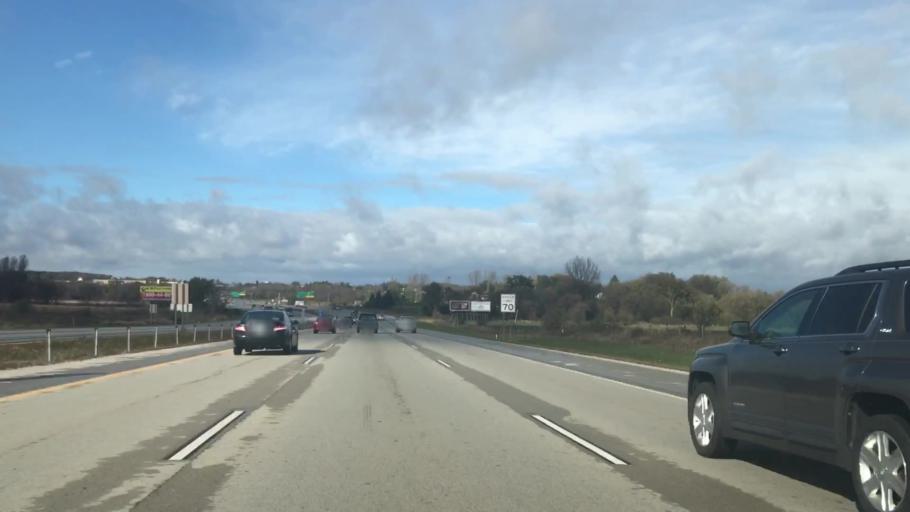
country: US
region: Wisconsin
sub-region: Washington County
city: Richfield
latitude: 43.2604
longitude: -88.1815
